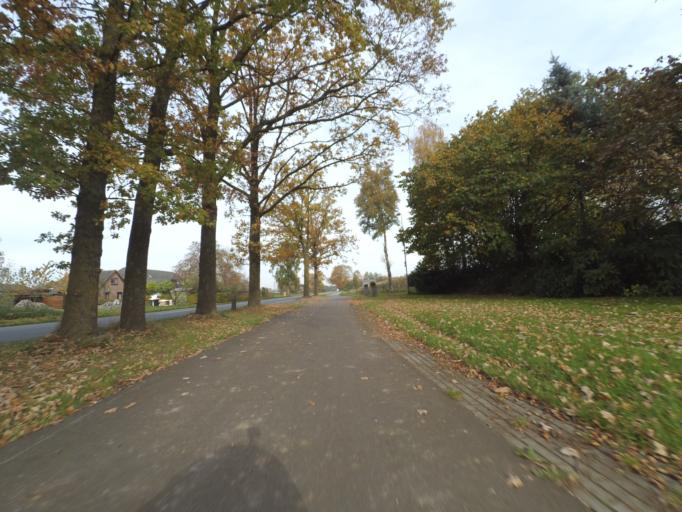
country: NL
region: Gelderland
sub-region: Gemeente Barneveld
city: Barneveld
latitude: 52.1165
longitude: 5.5570
